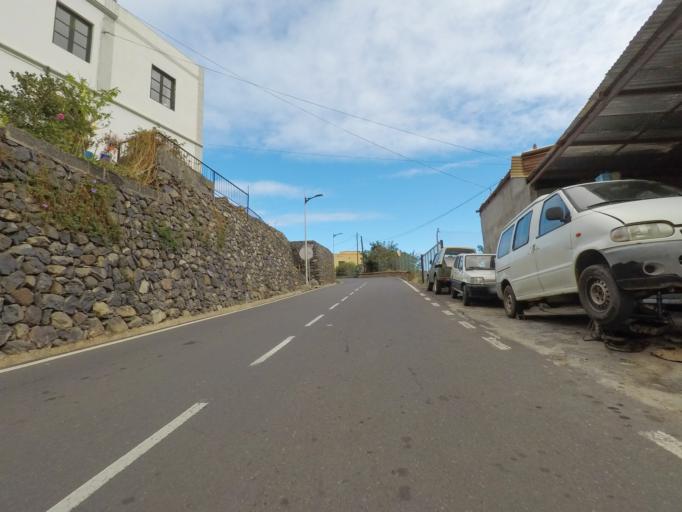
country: ES
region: Canary Islands
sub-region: Provincia de Santa Cruz de Tenerife
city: Hermigua
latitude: 28.1750
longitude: -17.1868
